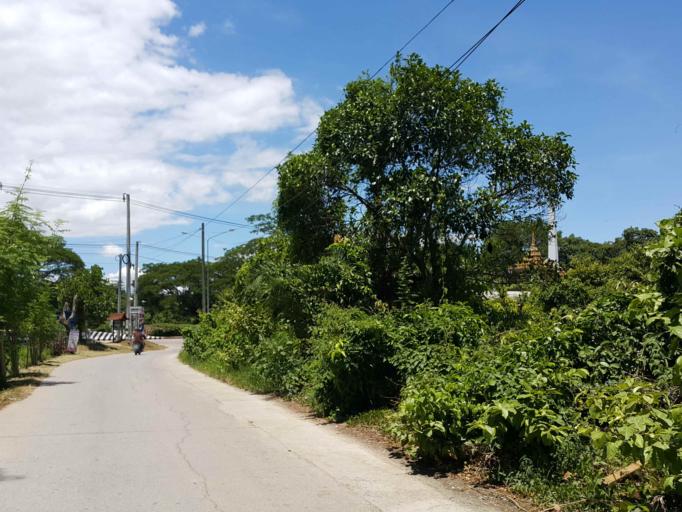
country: TH
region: Chiang Mai
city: Saraphi
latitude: 18.7488
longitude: 99.0204
